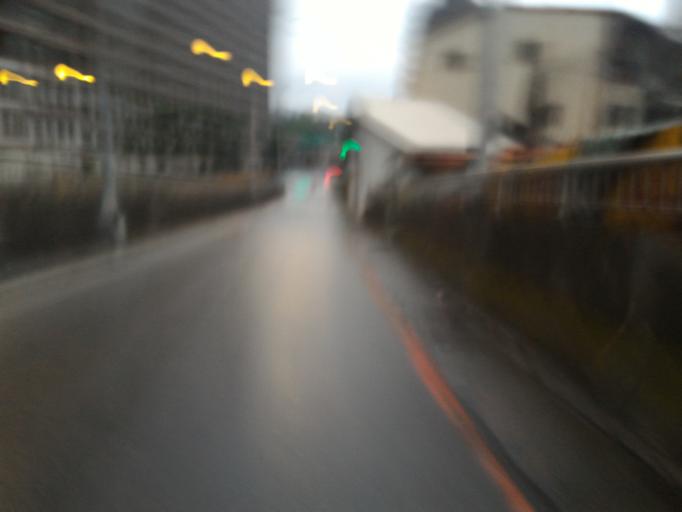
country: TW
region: Taipei
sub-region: Taipei
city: Banqiao
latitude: 24.9820
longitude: 121.4113
